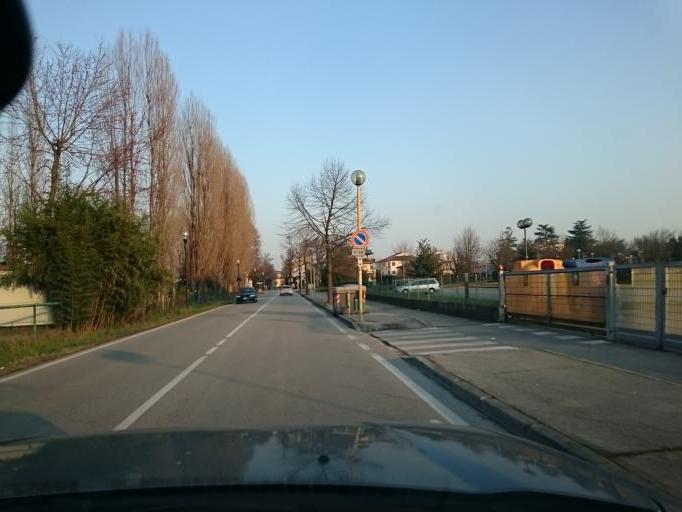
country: IT
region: Veneto
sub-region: Provincia di Padova
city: Abano Terme
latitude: 45.3619
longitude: 11.7830
